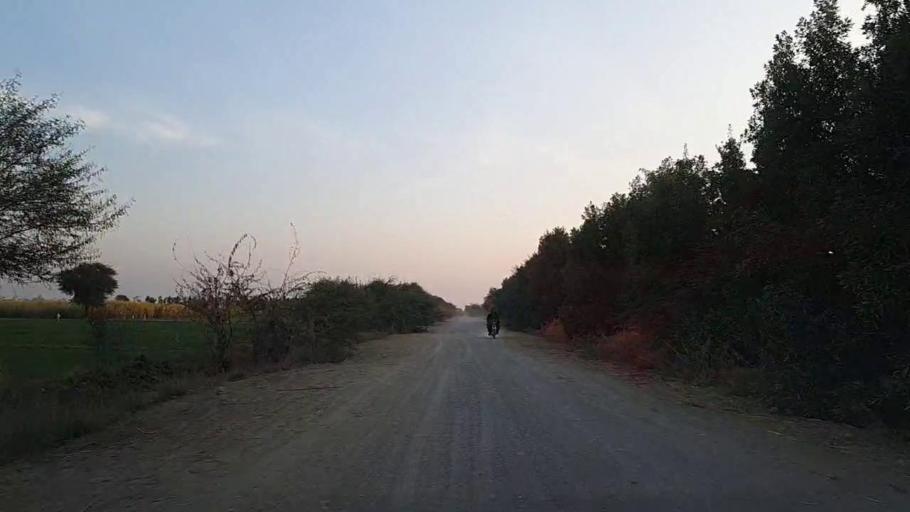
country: PK
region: Sindh
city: Tando Mittha Khan
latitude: 25.9670
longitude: 69.1104
